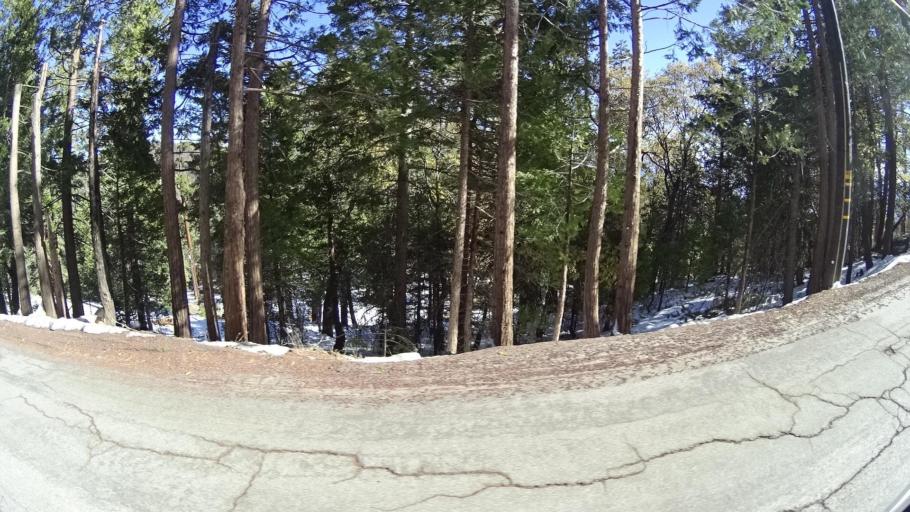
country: US
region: California
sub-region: Kern County
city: Alta Sierra
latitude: 35.7299
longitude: -118.5580
